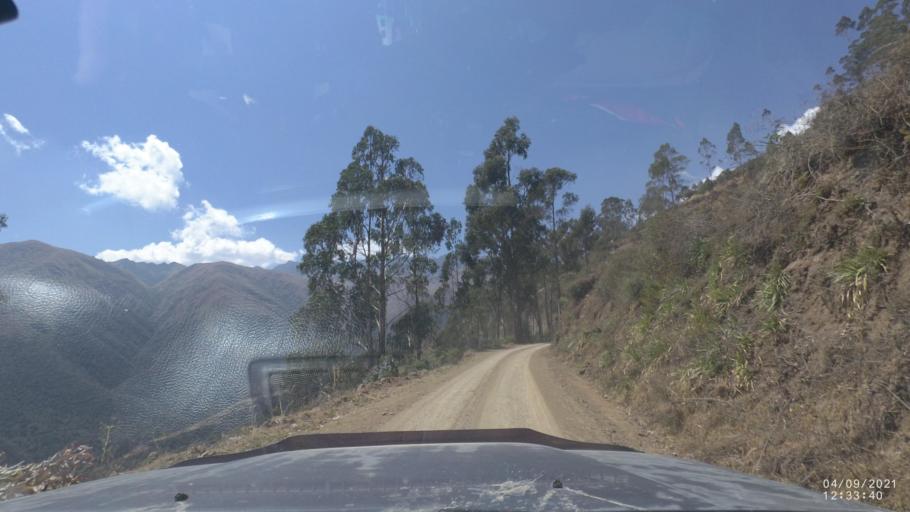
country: BO
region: Cochabamba
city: Colchani
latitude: -17.2232
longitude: -66.5175
